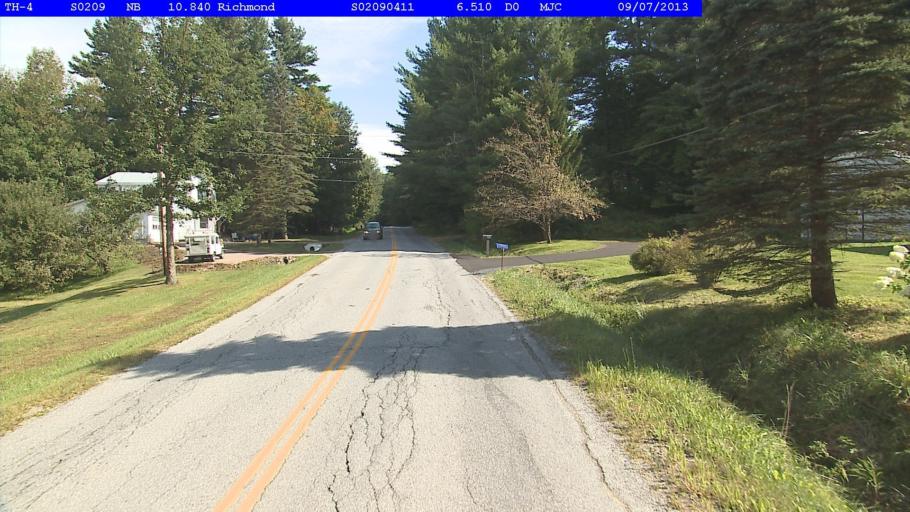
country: US
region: Vermont
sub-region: Chittenden County
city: Jericho
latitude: 44.4187
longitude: -72.9804
